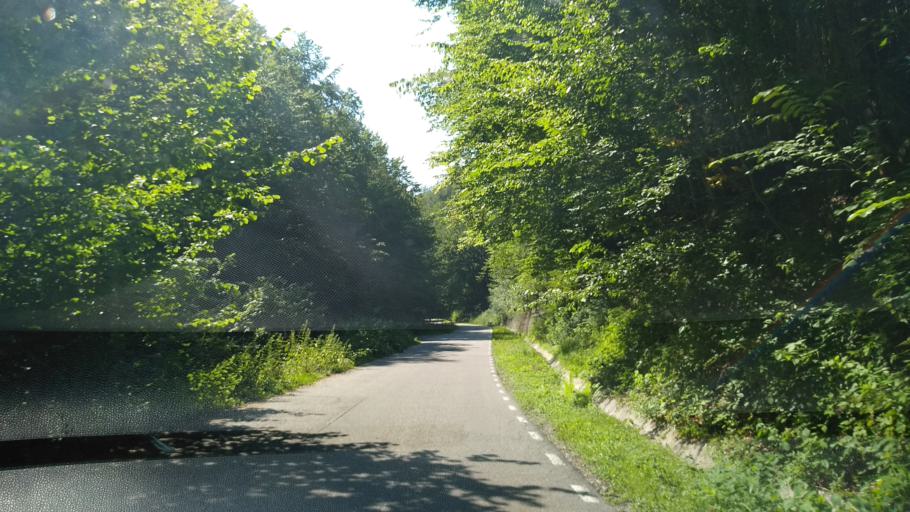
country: RO
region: Hunedoara
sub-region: Comuna Orastioara de Sus
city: Orastioara de Sus
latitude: 45.6213
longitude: 23.2753
